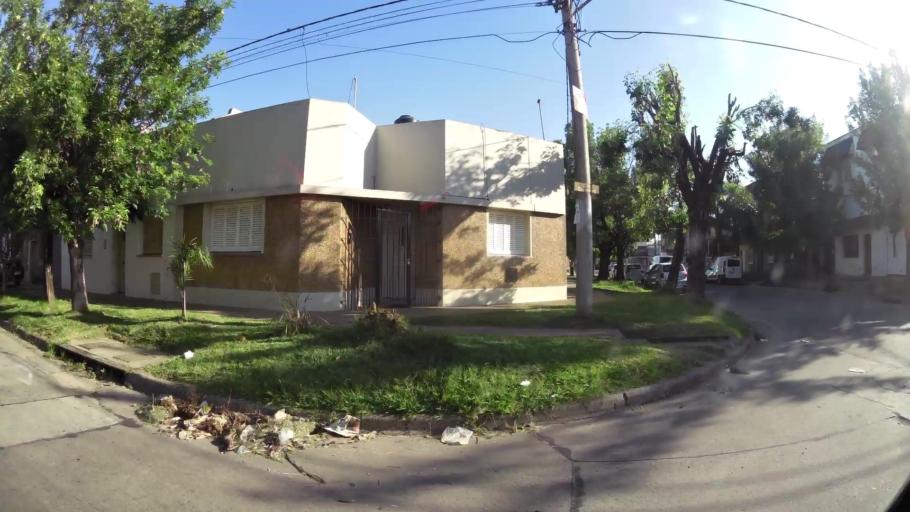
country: AR
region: Santa Fe
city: Santa Fe de la Vera Cruz
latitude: -31.6089
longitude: -60.6970
